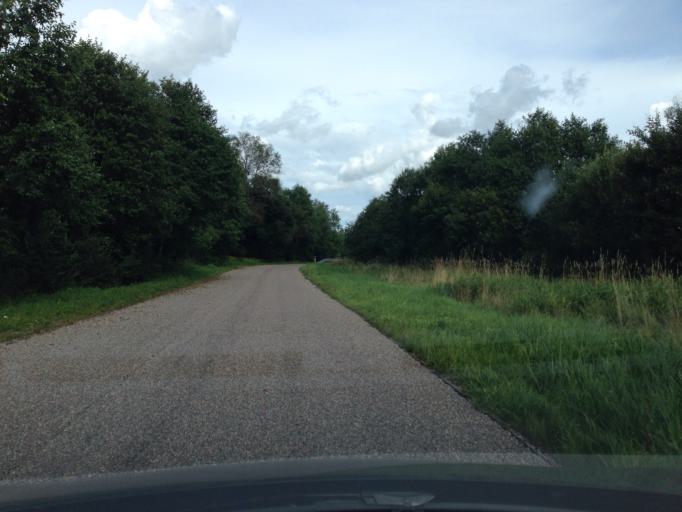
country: EE
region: Harju
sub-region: Saue linn
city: Saue
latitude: 59.2727
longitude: 24.5197
